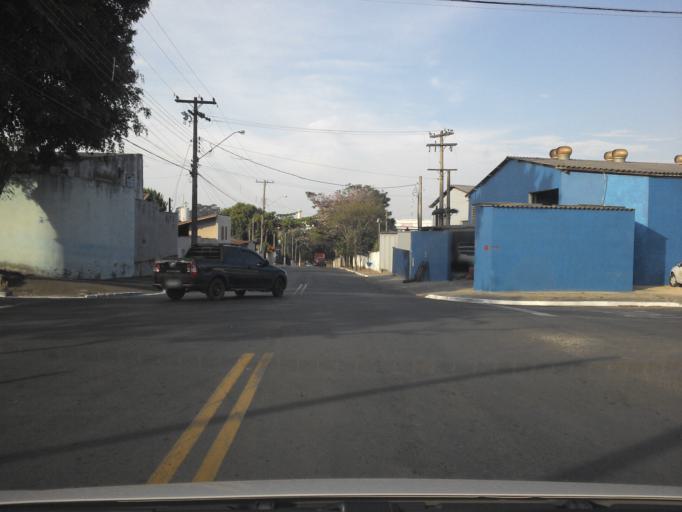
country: BR
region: Sao Paulo
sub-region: Hortolandia
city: Hortolandia
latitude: -22.9073
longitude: -47.2086
